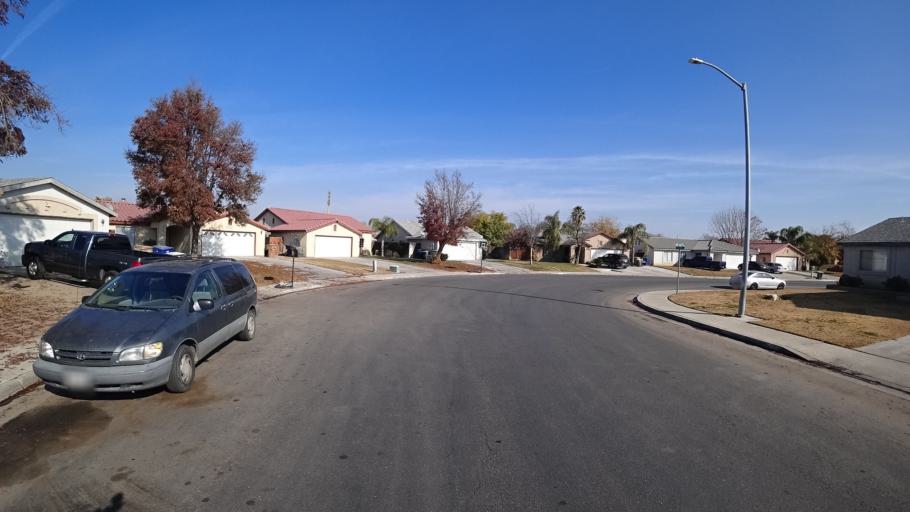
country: US
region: California
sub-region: Kern County
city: Greenfield
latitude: 35.3147
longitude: -119.0272
